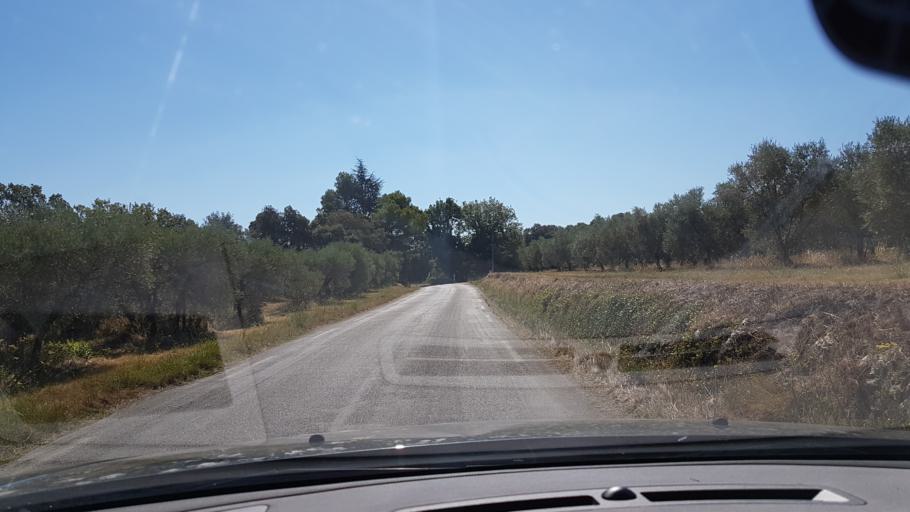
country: FR
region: Provence-Alpes-Cote d'Azur
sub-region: Departement des Bouches-du-Rhone
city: Eygalieres
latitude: 43.7634
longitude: 4.9322
